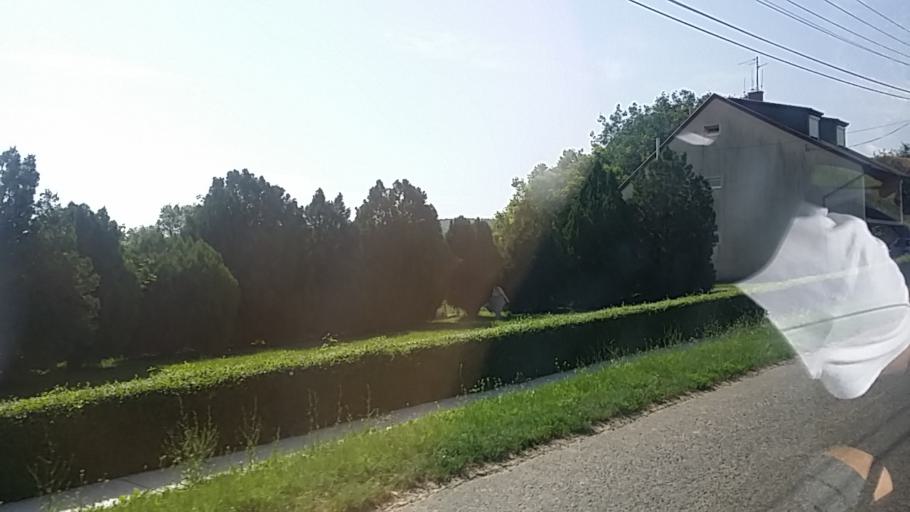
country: HU
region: Baranya
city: Siklos
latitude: 45.9065
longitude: 18.3333
